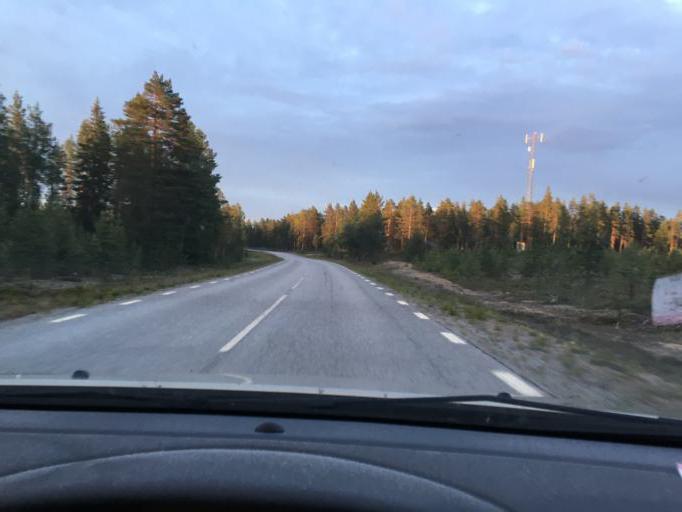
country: SE
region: Norrbotten
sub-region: Kalix Kommun
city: Toere
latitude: 66.0523
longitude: 22.4874
